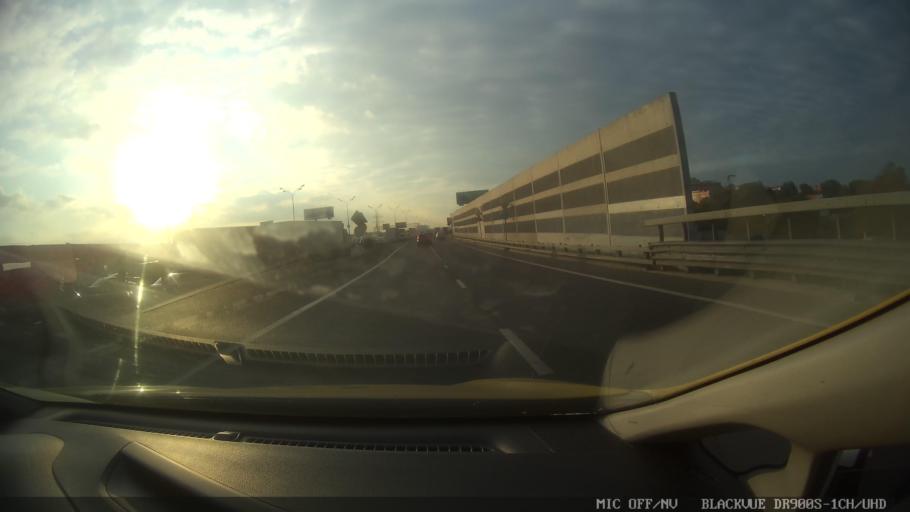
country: RU
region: Moscow
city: Yaroslavskiy
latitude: 55.8846
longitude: 37.7225
